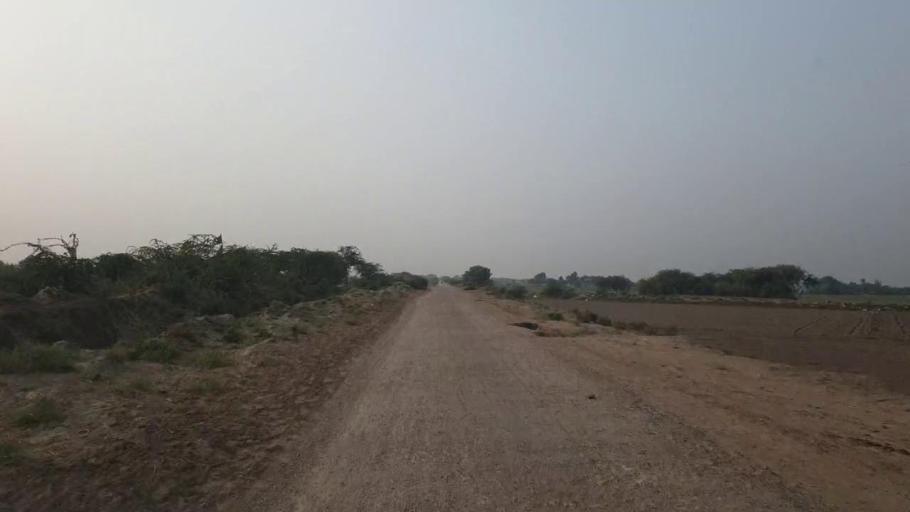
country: PK
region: Sindh
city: Mirpur Batoro
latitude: 24.6444
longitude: 68.3941
